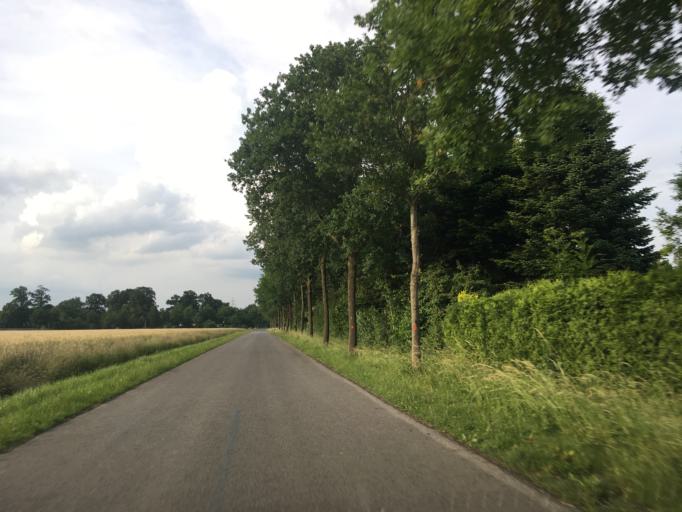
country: DE
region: North Rhine-Westphalia
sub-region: Regierungsbezirk Munster
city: Muenster
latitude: 51.9856
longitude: 7.5405
